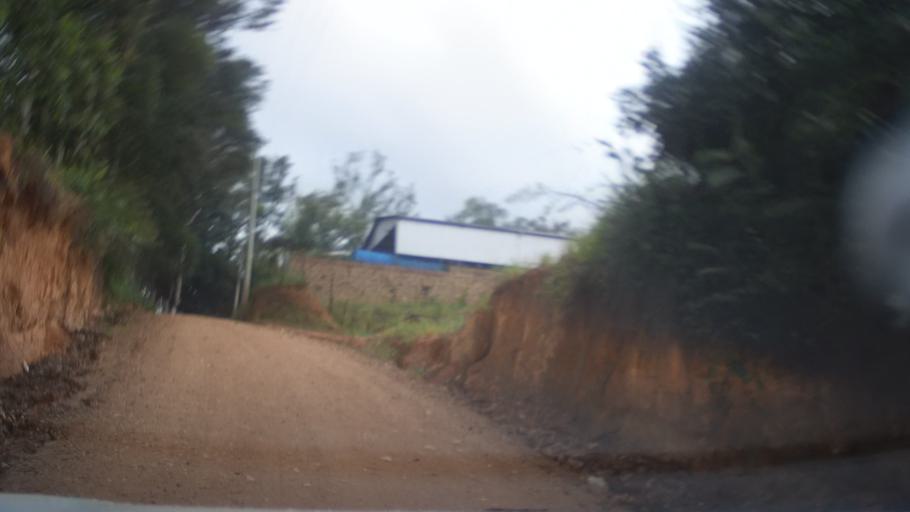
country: BR
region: Sao Paulo
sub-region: Itupeva
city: Itupeva
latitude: -23.1786
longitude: -47.0762
